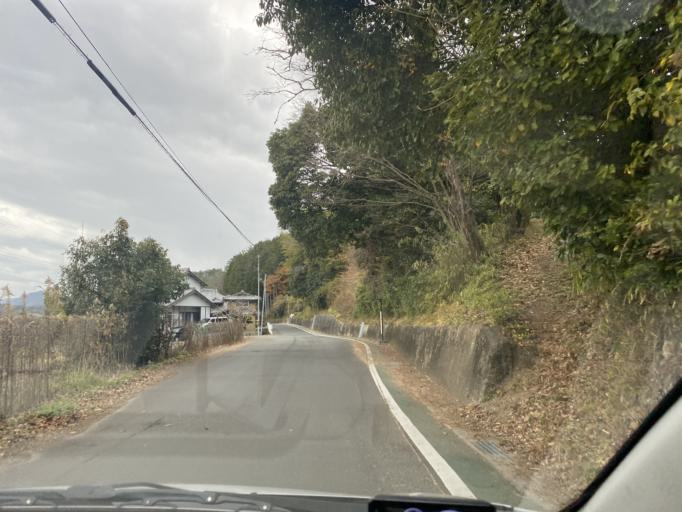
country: JP
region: Kyoto
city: Kameoka
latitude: 35.0512
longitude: 135.4778
